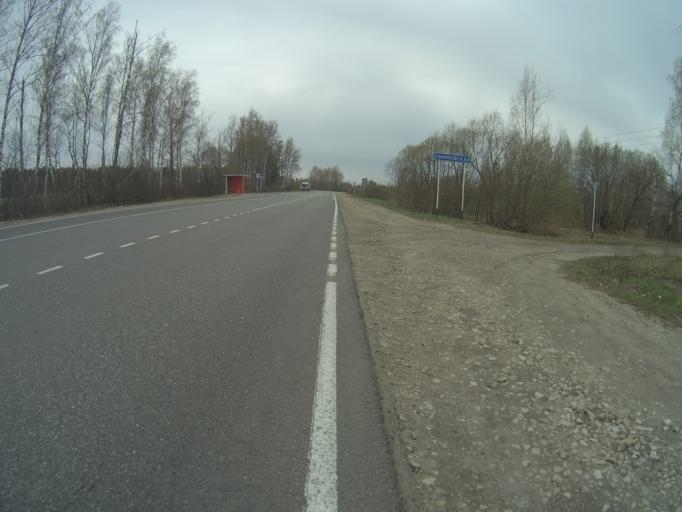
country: RU
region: Vladimir
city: Golovino
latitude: 55.9877
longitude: 40.5569
